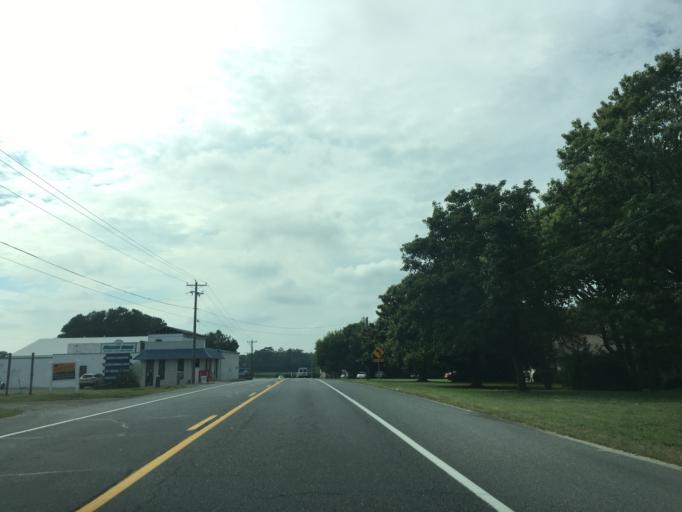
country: US
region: Delaware
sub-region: Sussex County
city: Long Neck
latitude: 38.5555
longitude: -75.1973
